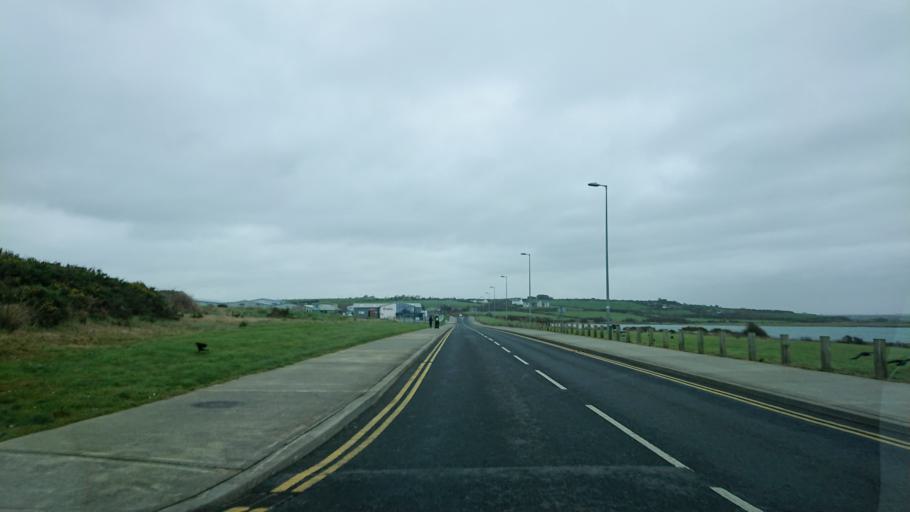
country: IE
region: Munster
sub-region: Waterford
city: Tra Mhor
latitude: 52.1644
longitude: -7.1337
